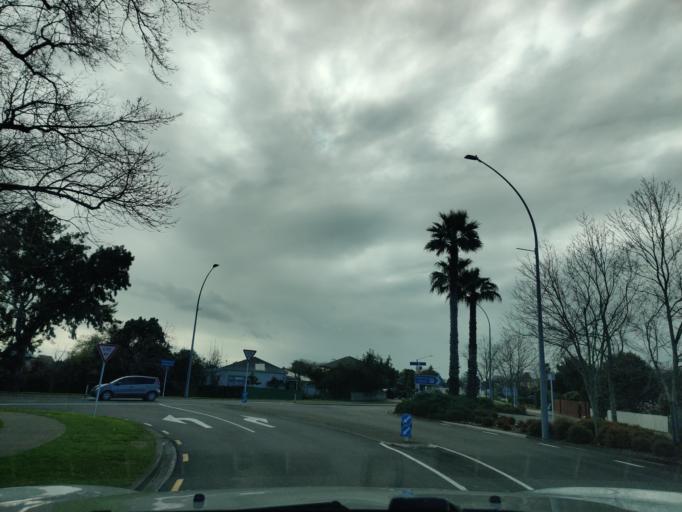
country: NZ
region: Hawke's Bay
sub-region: Hastings District
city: Hastings
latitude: -39.6687
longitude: 176.8814
